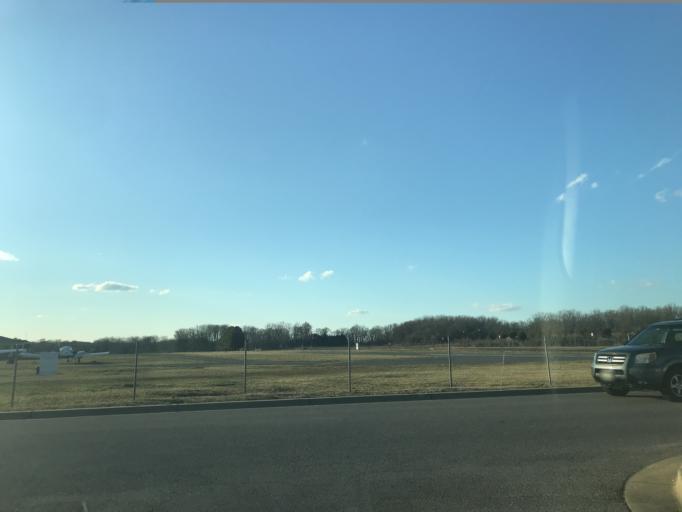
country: US
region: Maryland
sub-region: Anne Arundel County
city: Londontowne
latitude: 38.9412
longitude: -76.5639
